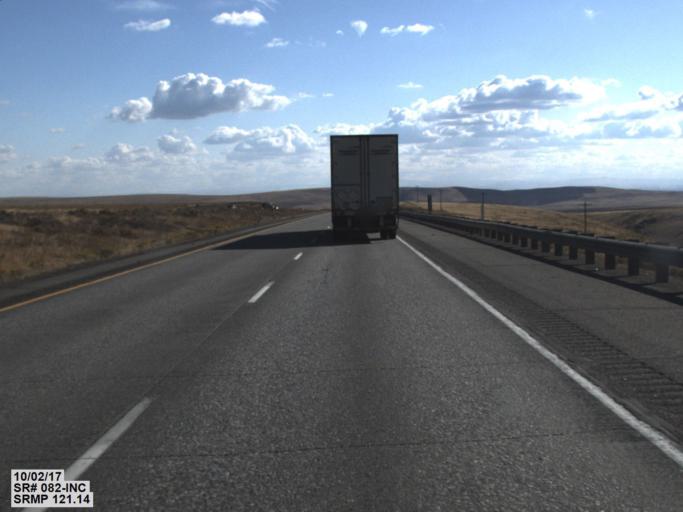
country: US
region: Washington
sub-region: Benton County
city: Highland
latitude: 46.0487
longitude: -119.2245
